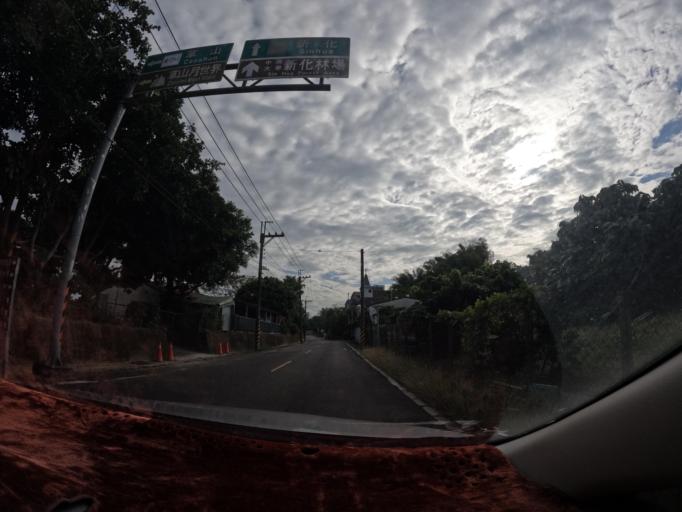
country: TW
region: Taiwan
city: Yujing
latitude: 23.0117
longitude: 120.4169
